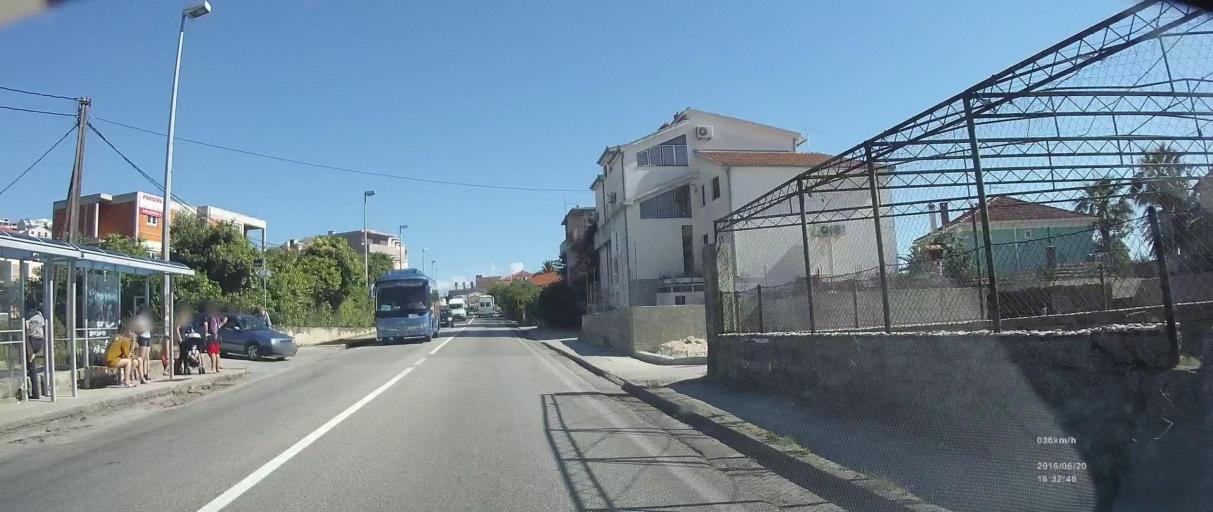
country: HR
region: Splitsko-Dalmatinska
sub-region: Grad Split
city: Stobrec
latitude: 43.5006
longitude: 16.5352
